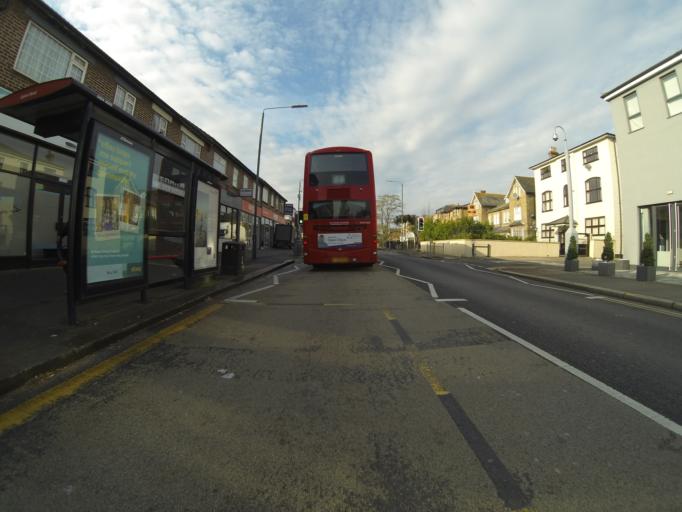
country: GB
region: England
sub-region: Greater London
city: Bexleyheath
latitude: 51.4584
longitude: 0.1321
